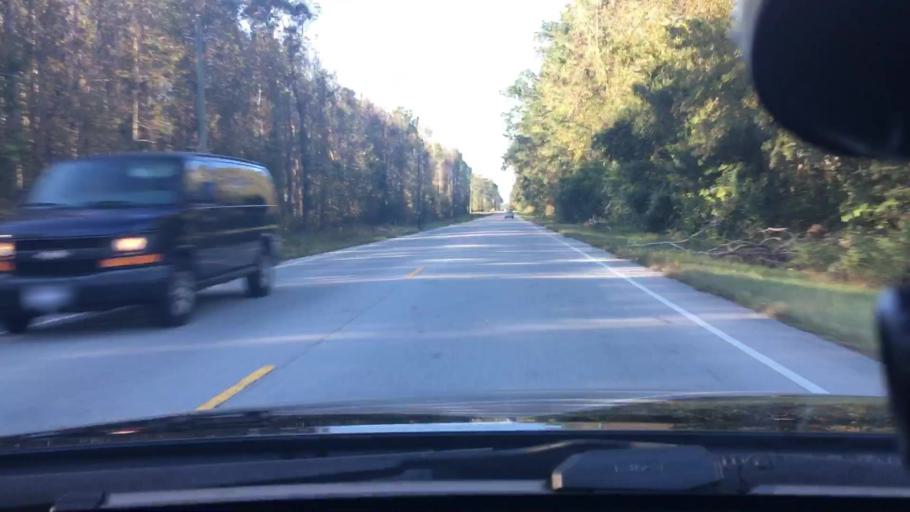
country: US
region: North Carolina
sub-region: Craven County
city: New Bern
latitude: 35.1999
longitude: -77.0564
